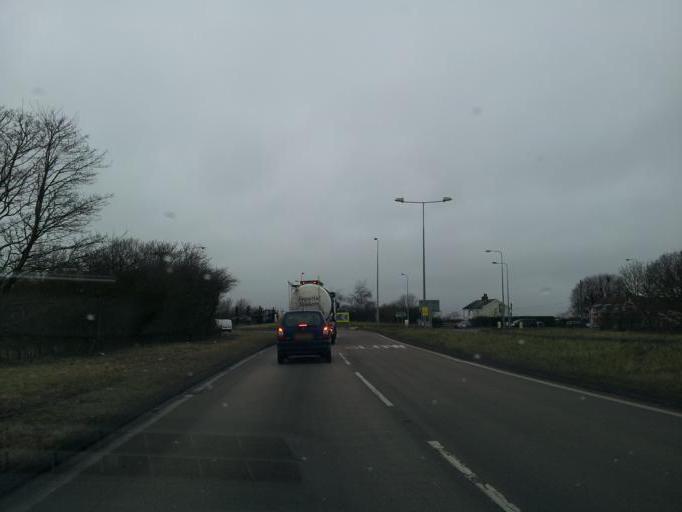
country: GB
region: England
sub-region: Essex
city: Mistley
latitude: 51.9042
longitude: 1.0874
